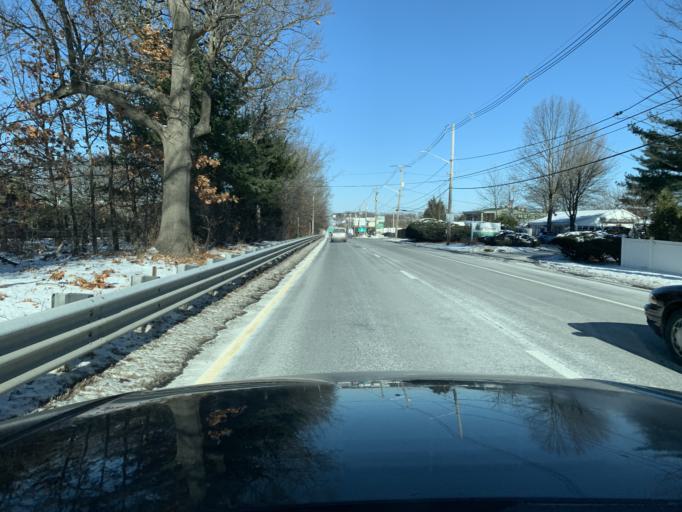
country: US
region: Massachusetts
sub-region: Essex County
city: South Peabody
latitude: 42.5523
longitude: -70.9812
